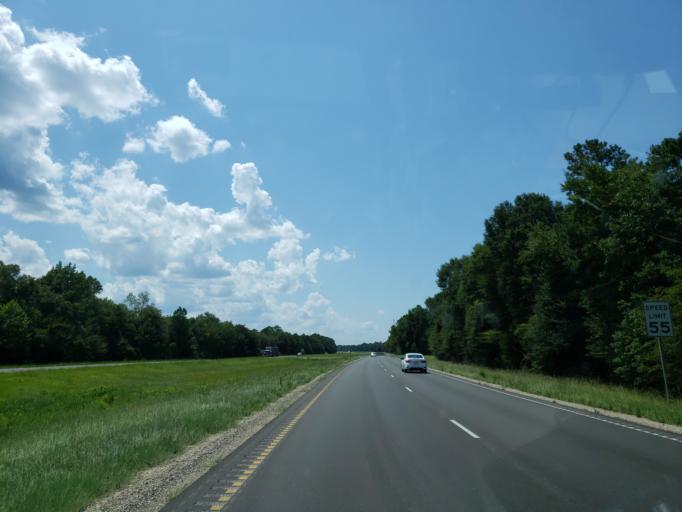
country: US
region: Mississippi
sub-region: Perry County
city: New Augusta
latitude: 31.2014
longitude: -89.0464
